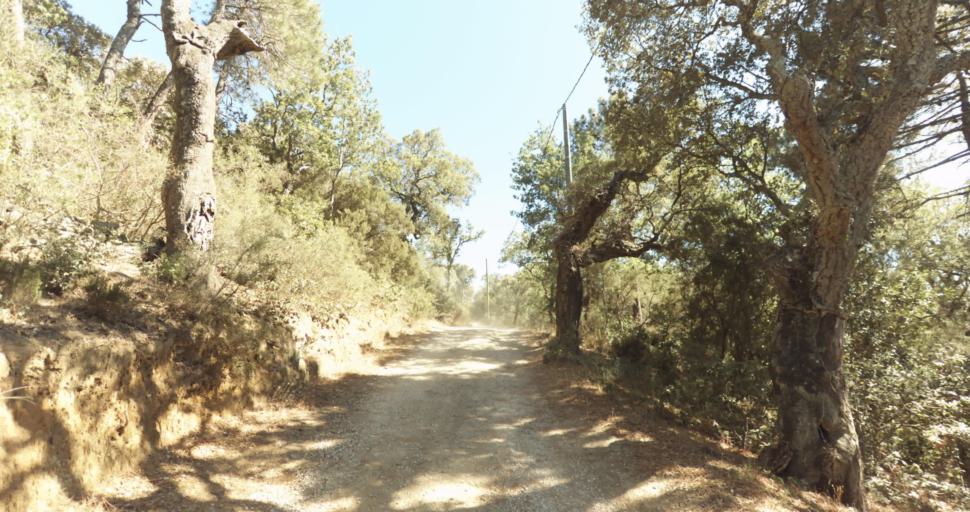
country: FR
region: Provence-Alpes-Cote d'Azur
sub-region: Departement du Var
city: Gassin
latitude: 43.2405
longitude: 6.5841
